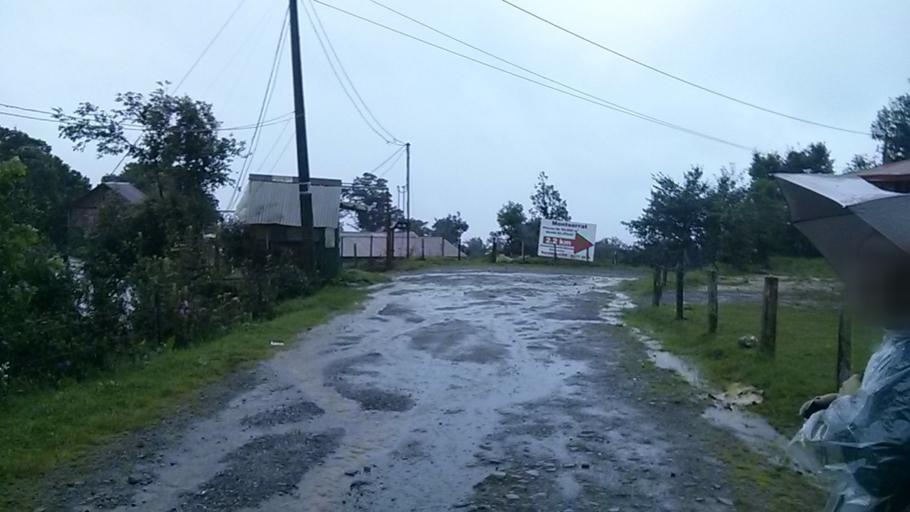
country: CR
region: San Jose
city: Ipis
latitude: 10.0283
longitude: -83.9435
